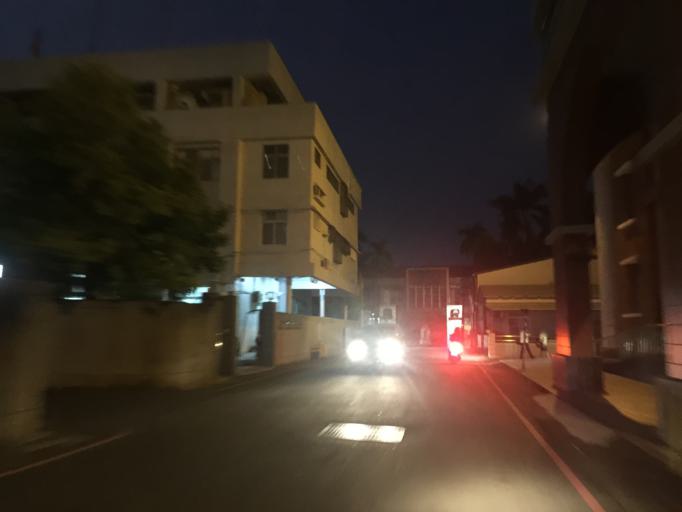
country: TW
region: Taiwan
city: Xinying
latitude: 23.3121
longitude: 120.3225
